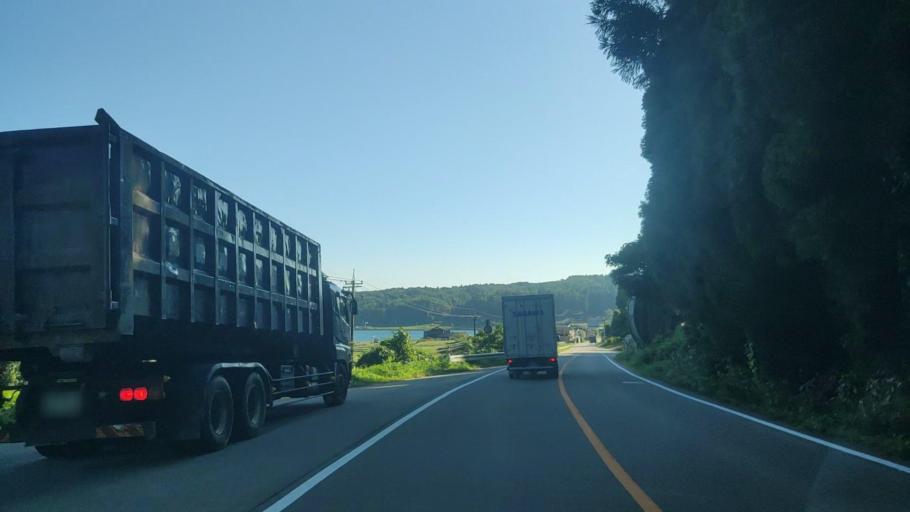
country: JP
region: Ishikawa
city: Nanao
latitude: 37.2074
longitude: 136.9086
